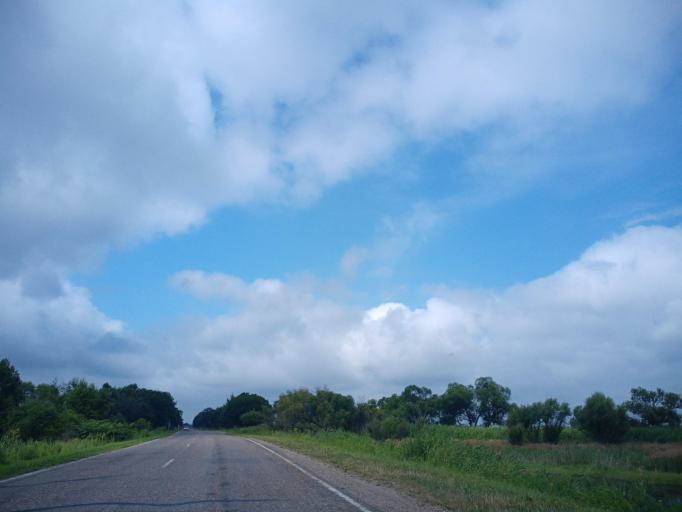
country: RU
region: Primorskiy
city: Dal'nerechensk
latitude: 45.9360
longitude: 133.8519
